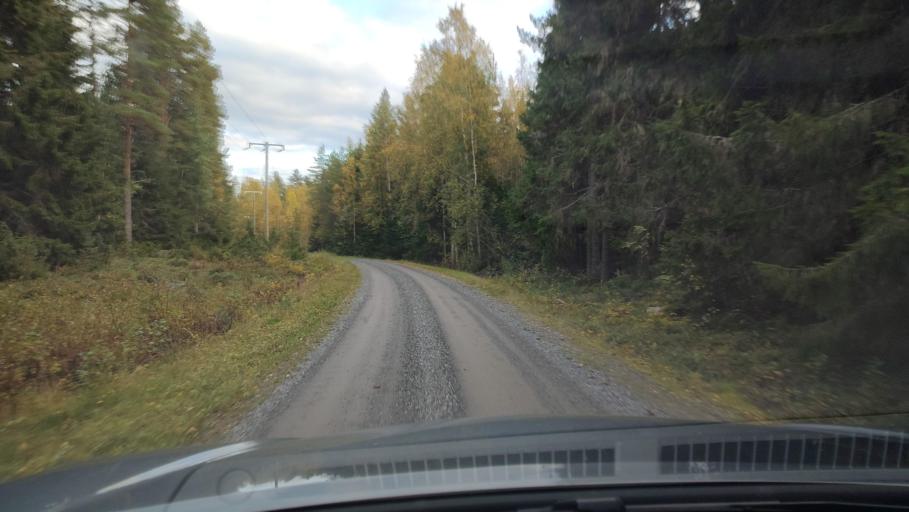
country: FI
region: Ostrobothnia
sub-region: Sydosterbotten
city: Kristinestad
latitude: 62.2326
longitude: 21.4021
